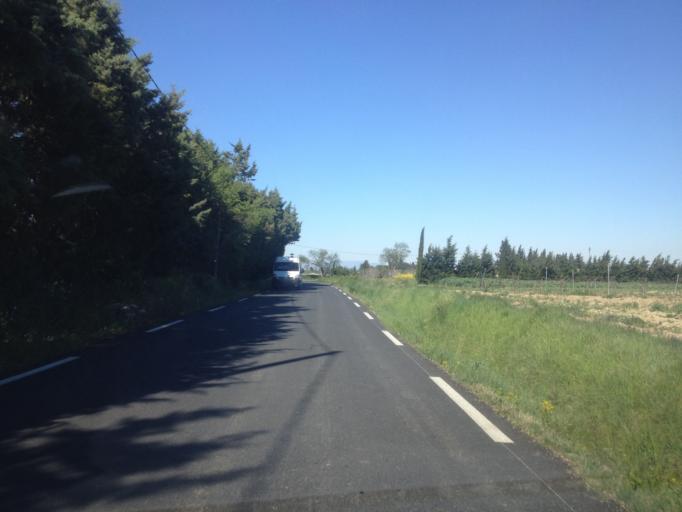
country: FR
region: Provence-Alpes-Cote d'Azur
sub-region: Departement du Vaucluse
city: Orange
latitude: 44.1539
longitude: 4.8173
